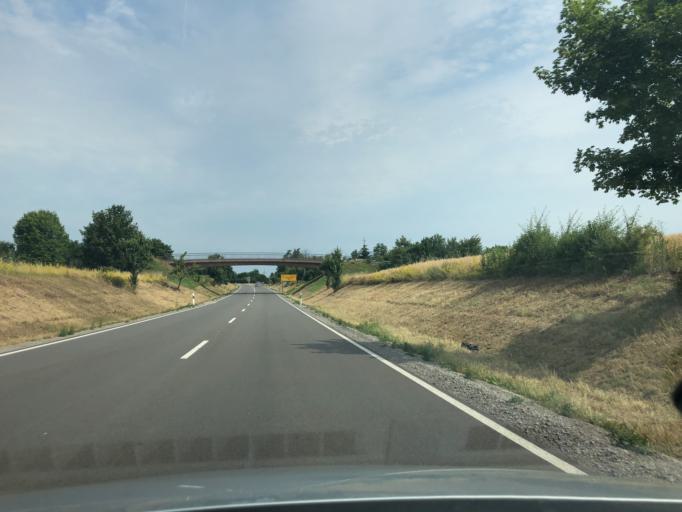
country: DE
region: Baden-Wuerttemberg
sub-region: Regierungsbezirk Stuttgart
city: Nufringen
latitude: 48.6394
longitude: 8.8819
